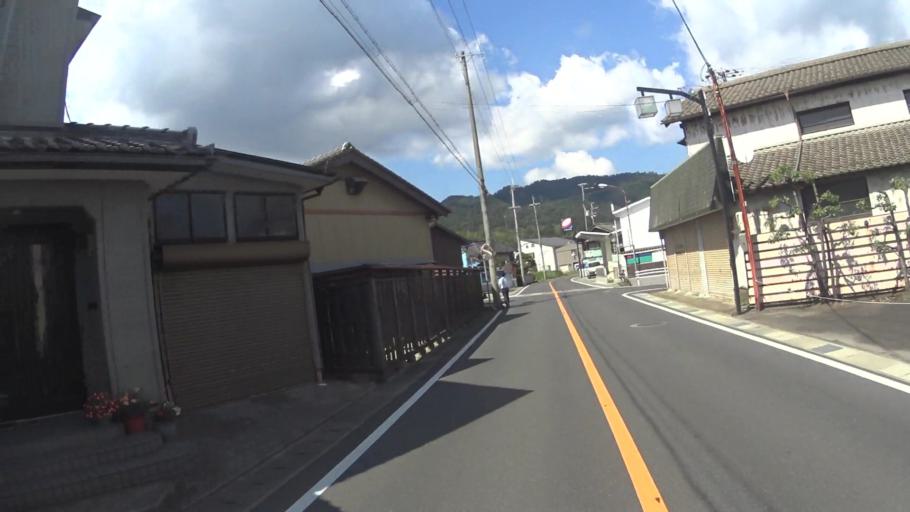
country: JP
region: Kyoto
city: Miyazu
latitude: 35.5633
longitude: 135.1528
